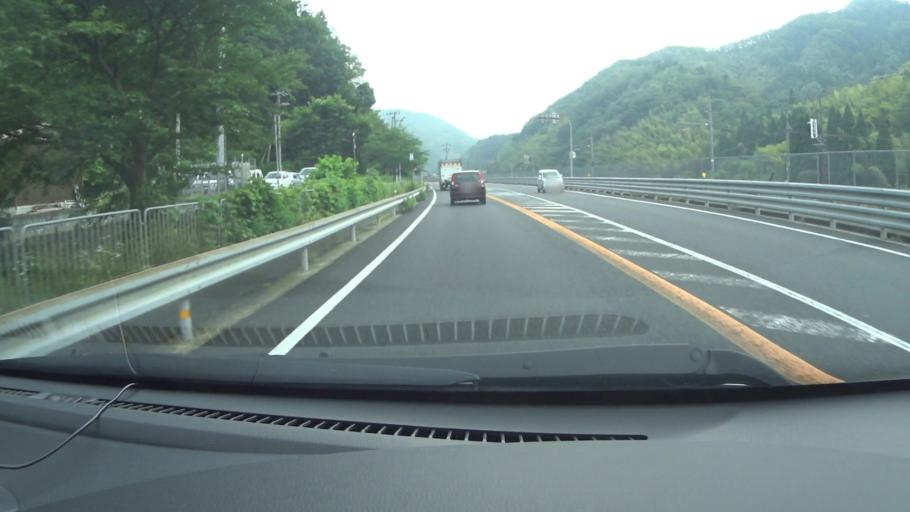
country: JP
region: Kyoto
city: Maizuru
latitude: 35.3989
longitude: 135.3203
